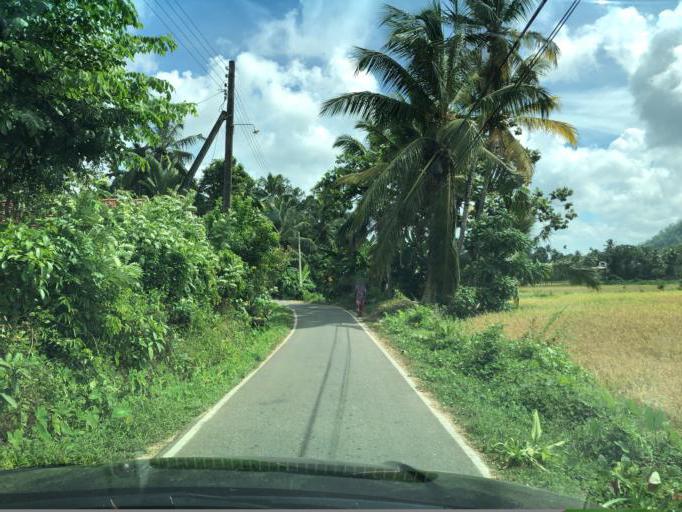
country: LK
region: Western
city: Horawala Junction
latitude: 6.5332
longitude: 80.0967
